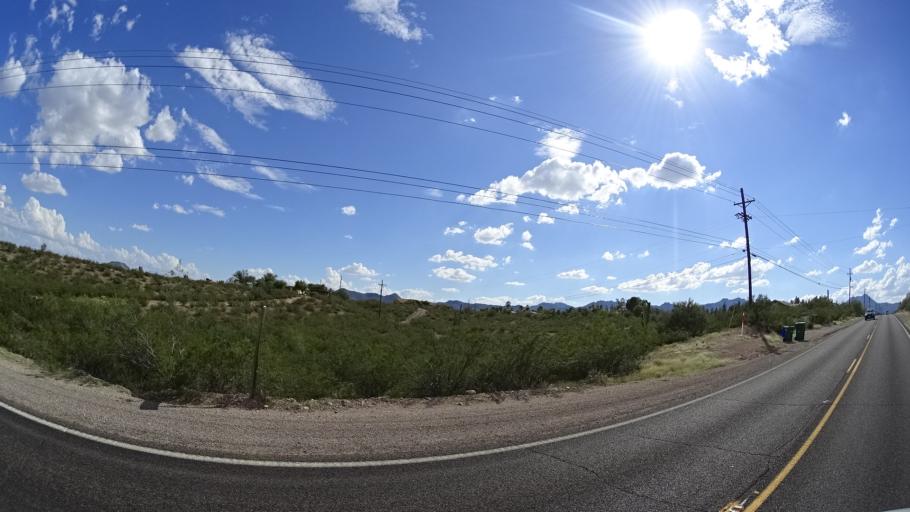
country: US
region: Arizona
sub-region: Pima County
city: Flowing Wells
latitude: 32.2797
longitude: -111.0357
